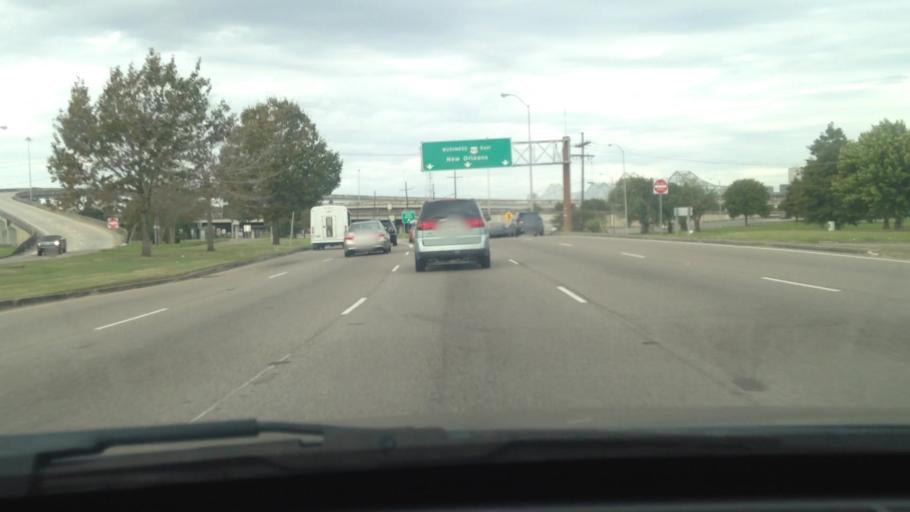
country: US
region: Louisiana
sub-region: Jefferson Parish
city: Terrytown
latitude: 29.9303
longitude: -90.0340
